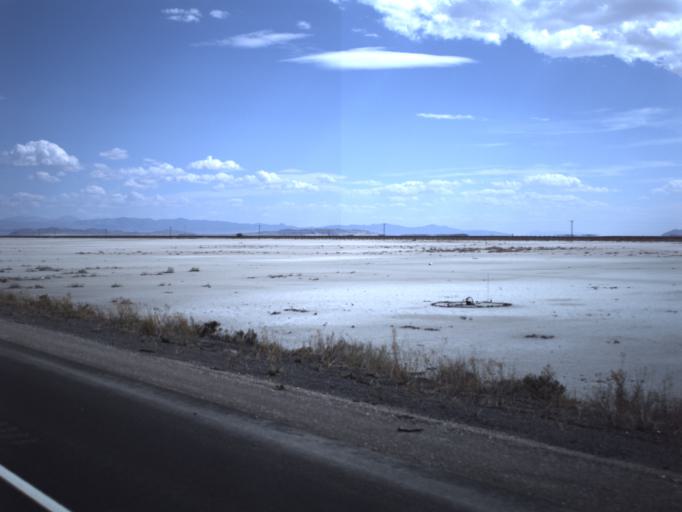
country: US
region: Utah
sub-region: Tooele County
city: Wendover
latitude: 40.7303
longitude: -113.4764
